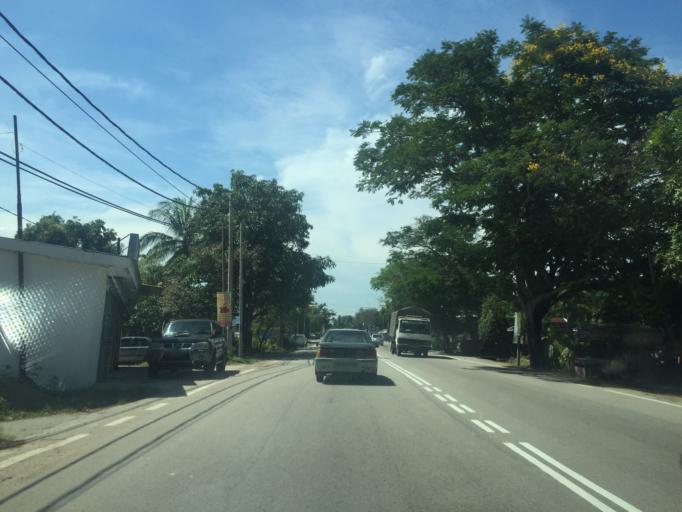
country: MY
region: Penang
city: Permatang Kuching
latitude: 5.4481
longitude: 100.4318
